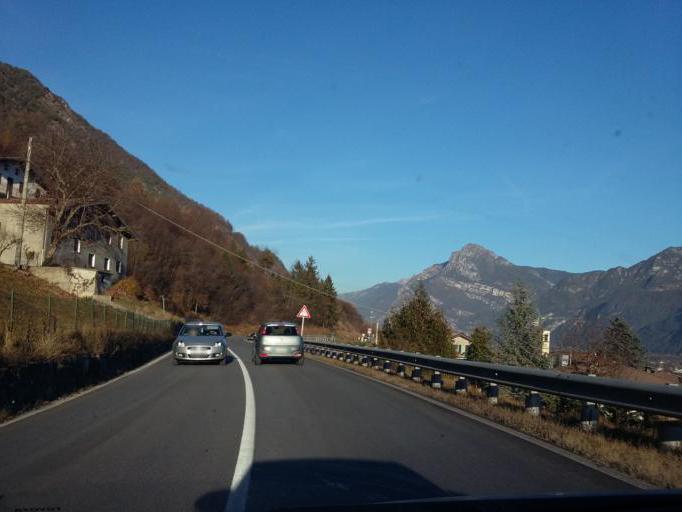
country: IT
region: Lombardy
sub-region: Provincia di Brescia
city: Ponte Caffaro
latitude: 45.8118
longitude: 10.5144
